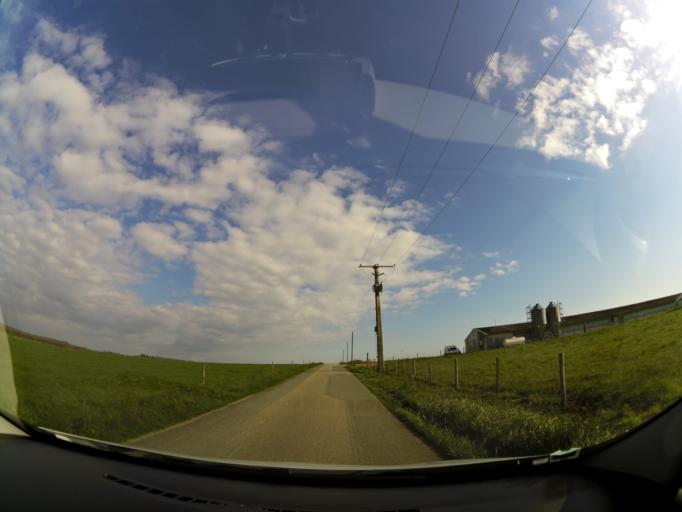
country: FR
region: Brittany
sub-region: Departement d'Ille-et-Vilaine
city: Laille
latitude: 47.9493
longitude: -1.6984
